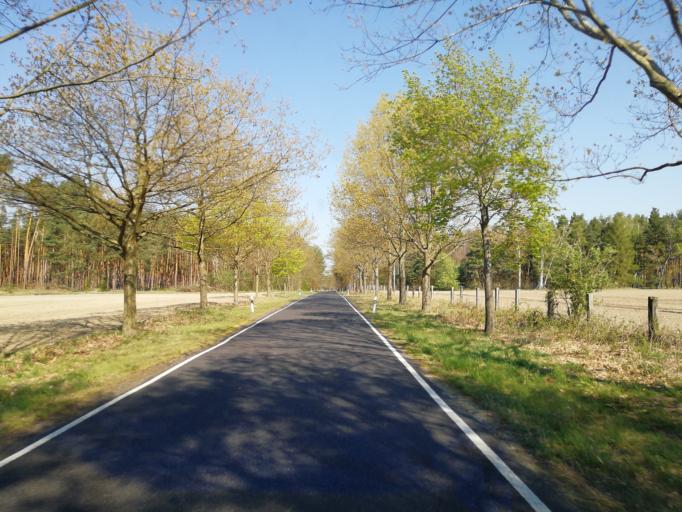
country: DE
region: Brandenburg
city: Bronkow
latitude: 51.7126
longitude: 13.8676
